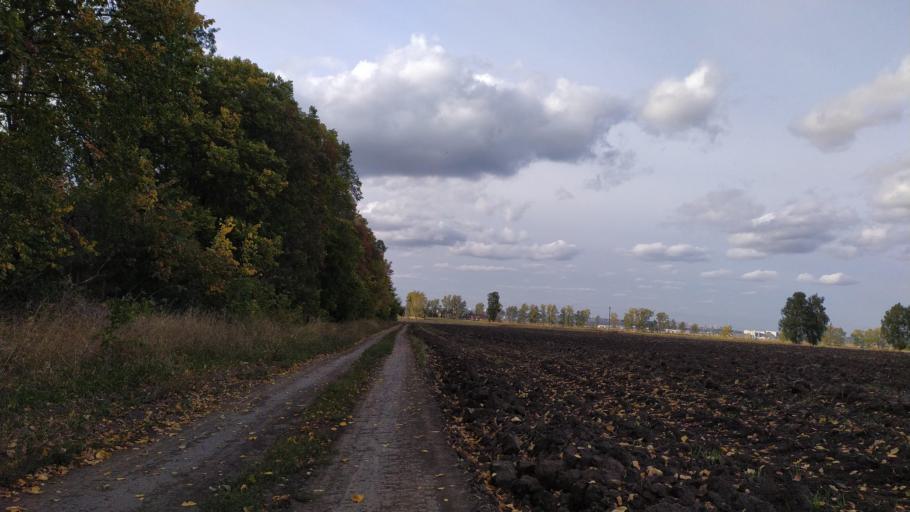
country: RU
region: Kursk
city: Kursk
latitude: 51.6228
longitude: 36.1615
